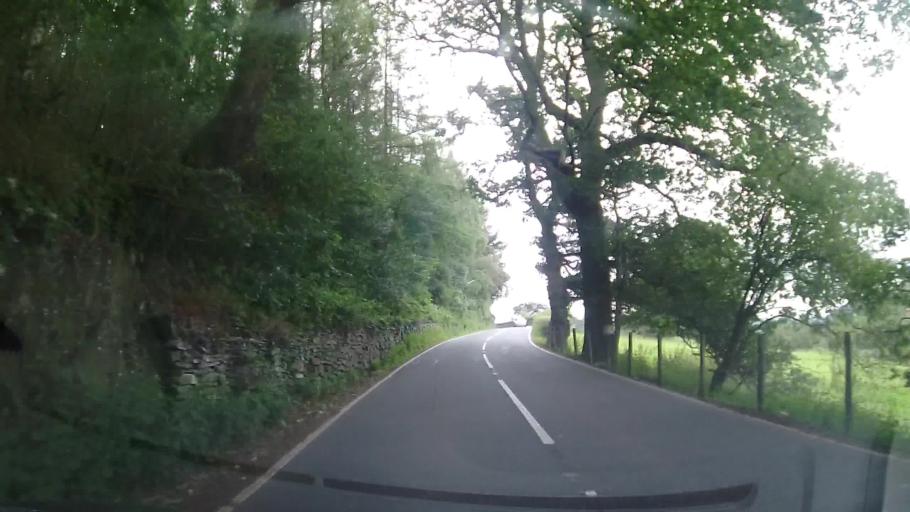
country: GB
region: Wales
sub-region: Denbighshire
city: Llandrillo
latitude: 52.9441
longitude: -3.4188
